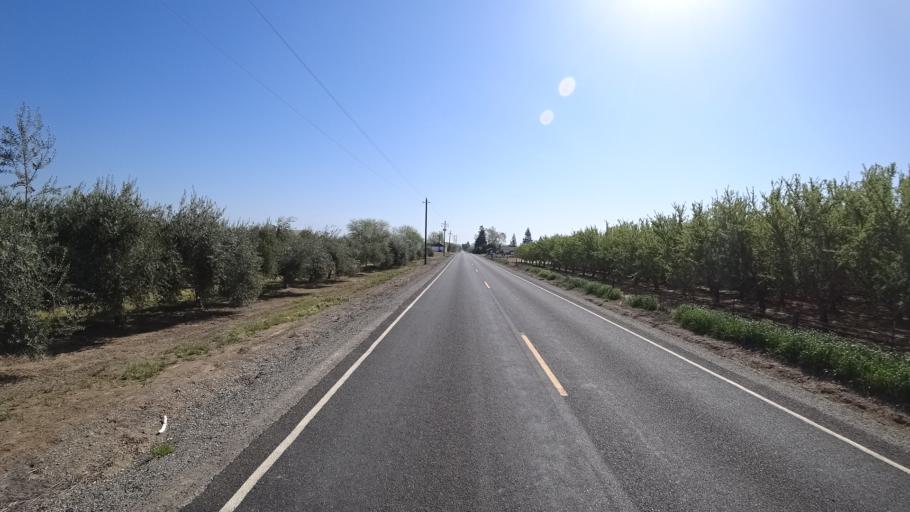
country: US
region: California
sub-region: Glenn County
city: Hamilton City
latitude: 39.6596
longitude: -122.0118
